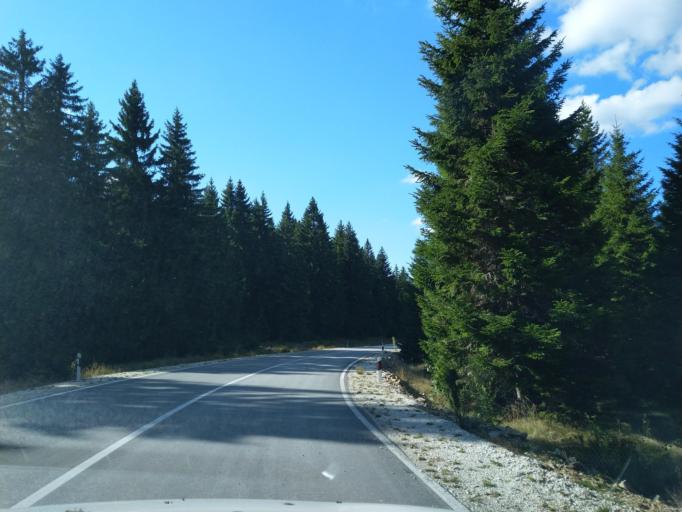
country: RS
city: Sokolovica
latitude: 43.2830
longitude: 20.3264
